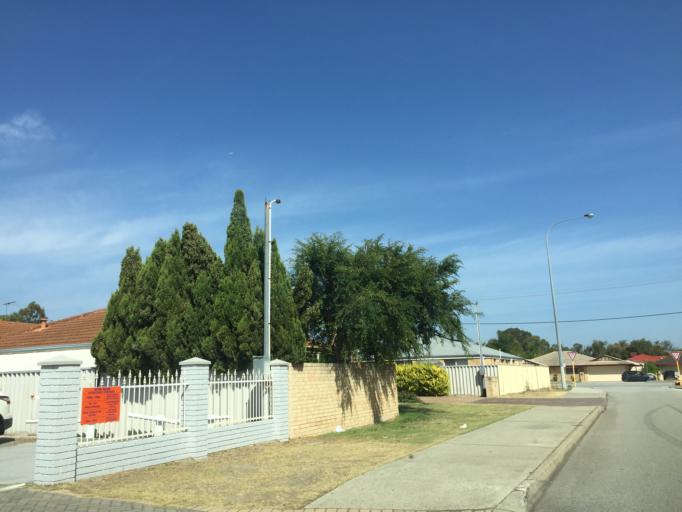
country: AU
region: Western Australia
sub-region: Gosnells
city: Thornlie
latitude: -32.0788
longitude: 115.9579
